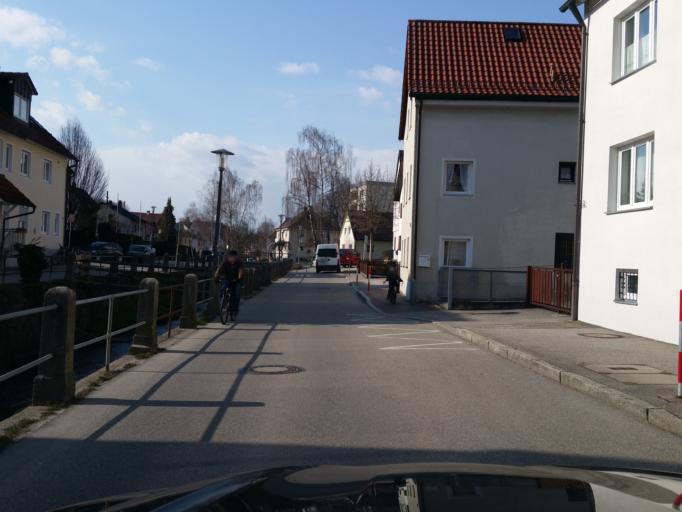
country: DE
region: Bavaria
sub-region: Lower Bavaria
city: Landshut
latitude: 48.5231
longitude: 12.1438
